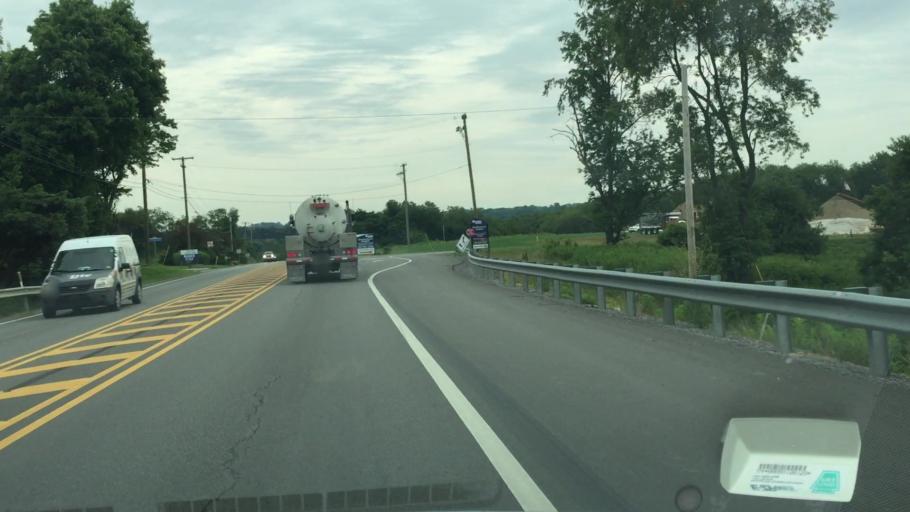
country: US
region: Pennsylvania
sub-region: Butler County
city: Mars
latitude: 40.6961
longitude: -79.9644
